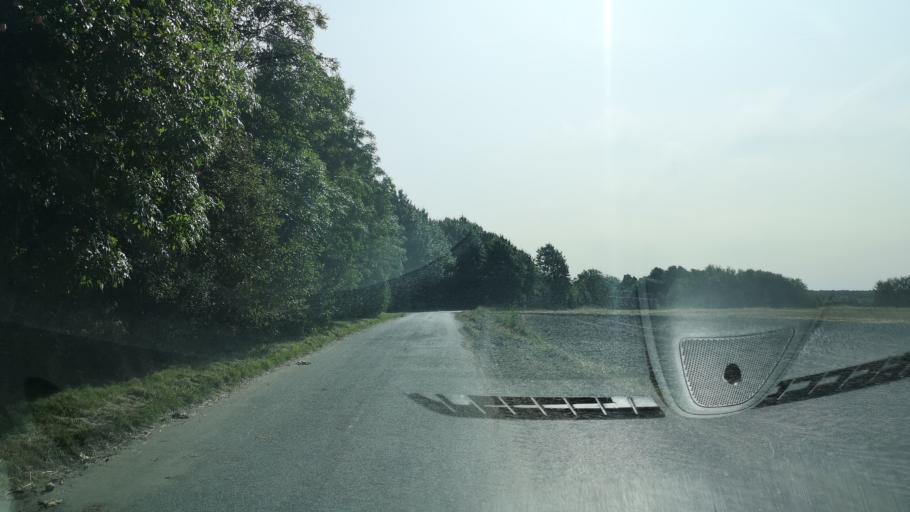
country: DK
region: Central Jutland
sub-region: Herning Kommune
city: Herning
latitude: 56.1707
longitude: 8.9565
